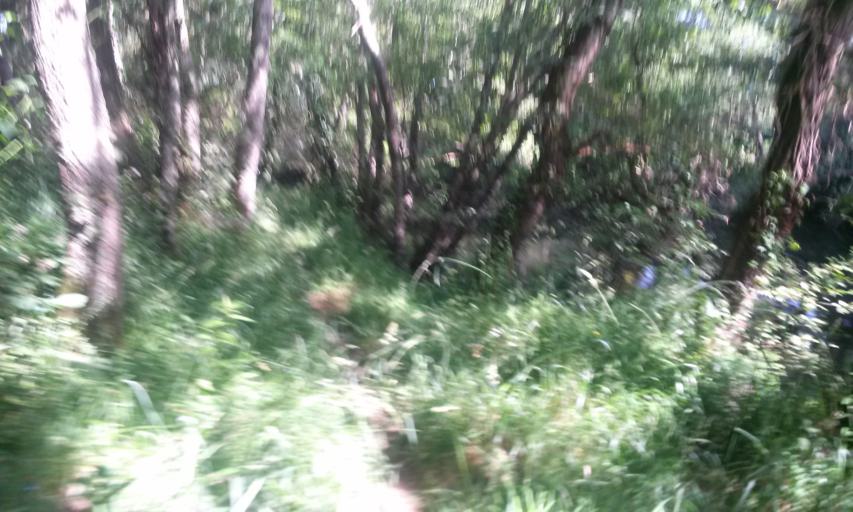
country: ES
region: Galicia
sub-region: Provincia de Lugo
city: Begonte
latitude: 43.1692
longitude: -7.7544
